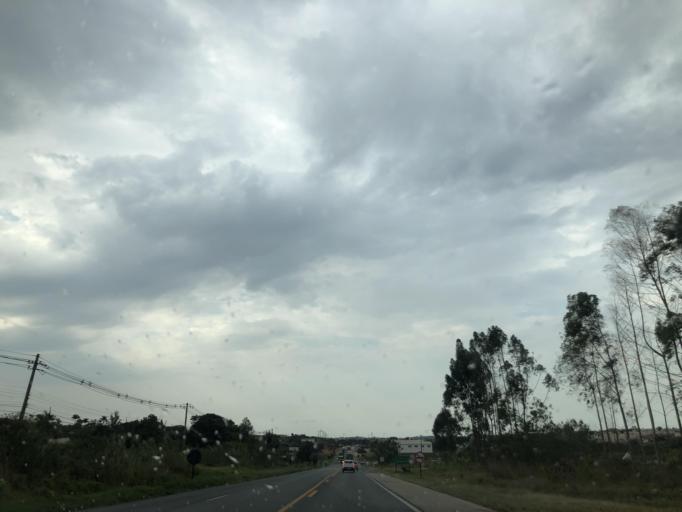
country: BR
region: Sao Paulo
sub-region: Salto De Pirapora
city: Salto de Pirapora
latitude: -23.6505
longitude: -47.5850
